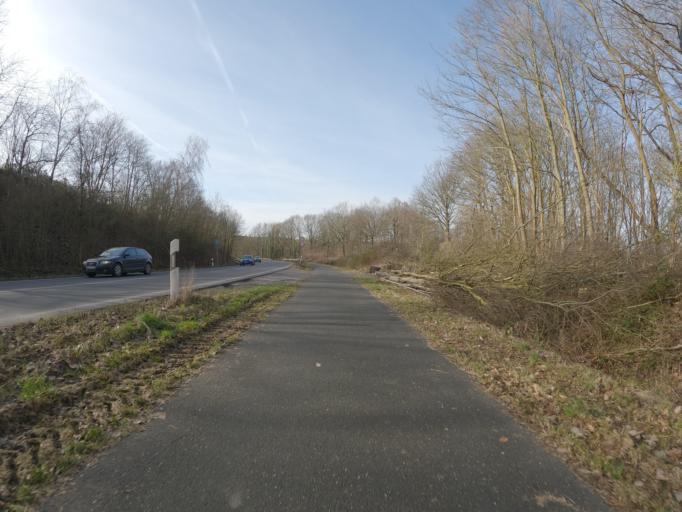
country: DE
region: North Rhine-Westphalia
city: Stolberg
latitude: 50.7608
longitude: 6.2111
